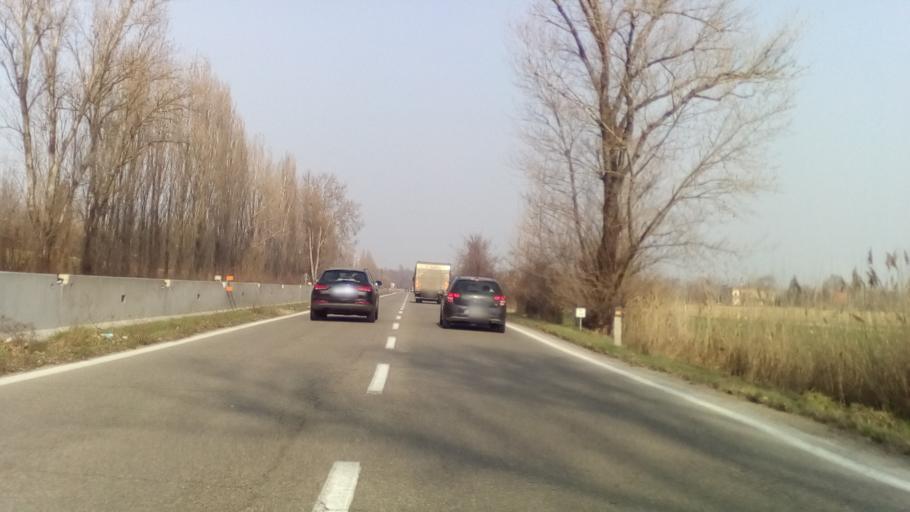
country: IT
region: Emilia-Romagna
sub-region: Provincia di Modena
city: Modena
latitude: 44.6191
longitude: 10.9429
